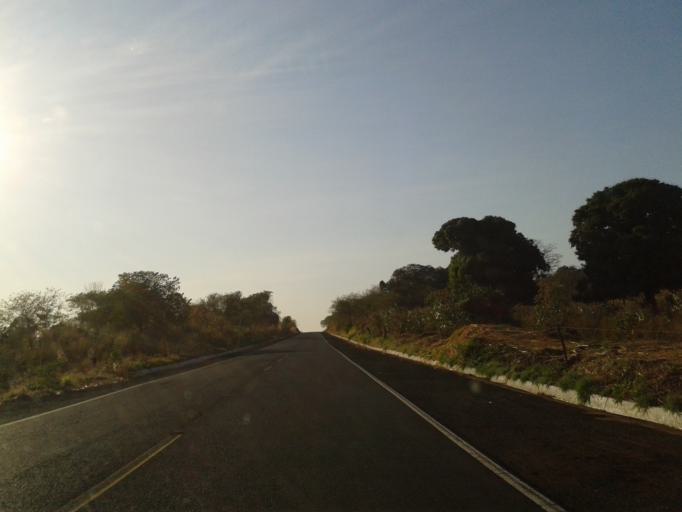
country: BR
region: Minas Gerais
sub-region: Santa Vitoria
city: Santa Vitoria
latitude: -19.1689
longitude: -50.0652
